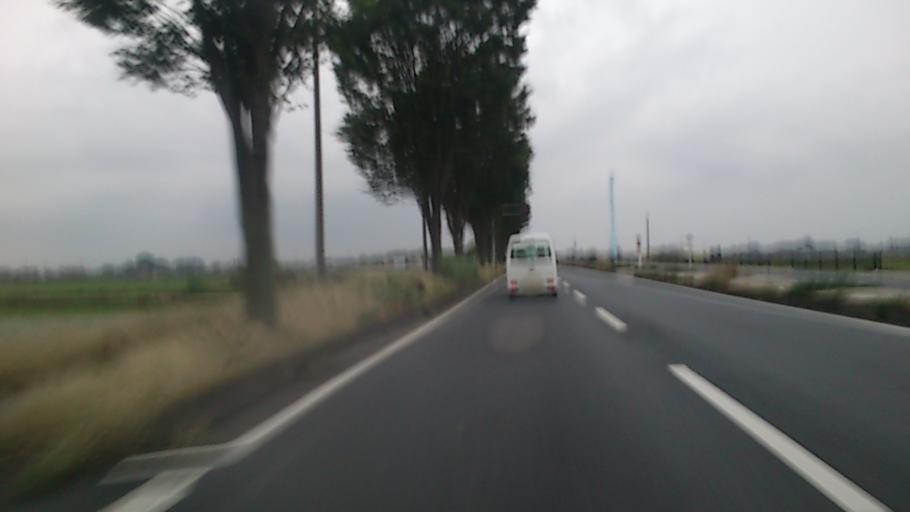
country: JP
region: Saitama
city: Hanyu
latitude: 36.1555
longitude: 139.4988
